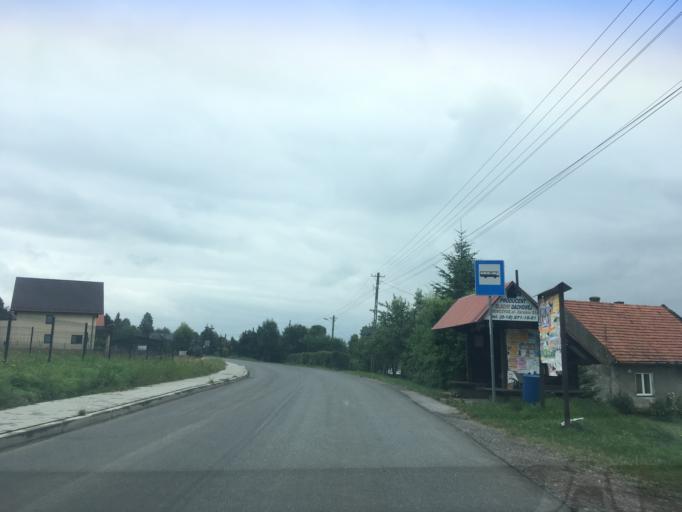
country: PL
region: Lesser Poland Voivodeship
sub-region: Powiat myslenicki
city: Dobczyce
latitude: 49.8603
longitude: 20.0895
